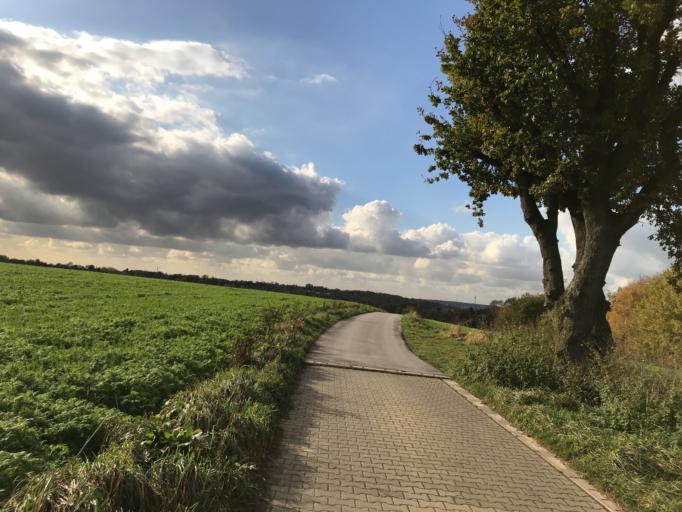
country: DE
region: North Rhine-Westphalia
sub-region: Regierungsbezirk Dusseldorf
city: Muelheim (Ruhr)
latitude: 51.4246
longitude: 6.9314
